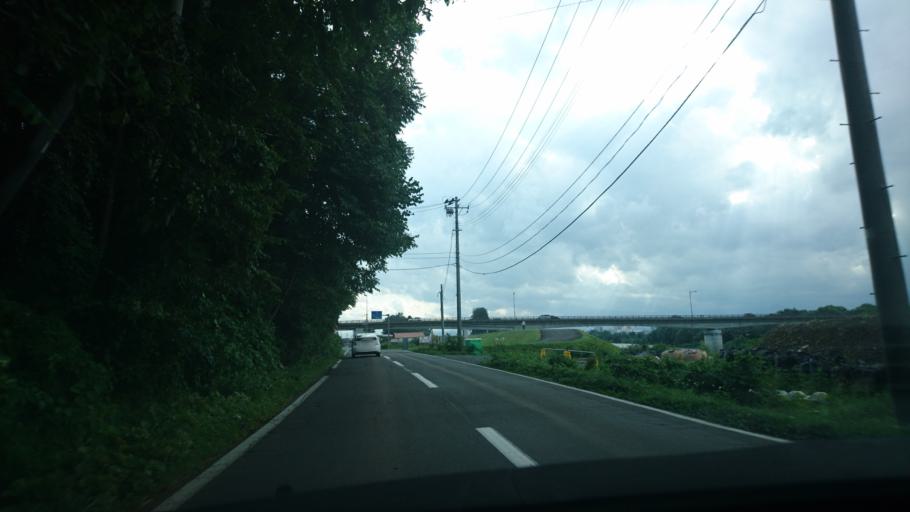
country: JP
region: Iwate
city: Kitakami
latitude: 39.2907
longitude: 141.1425
